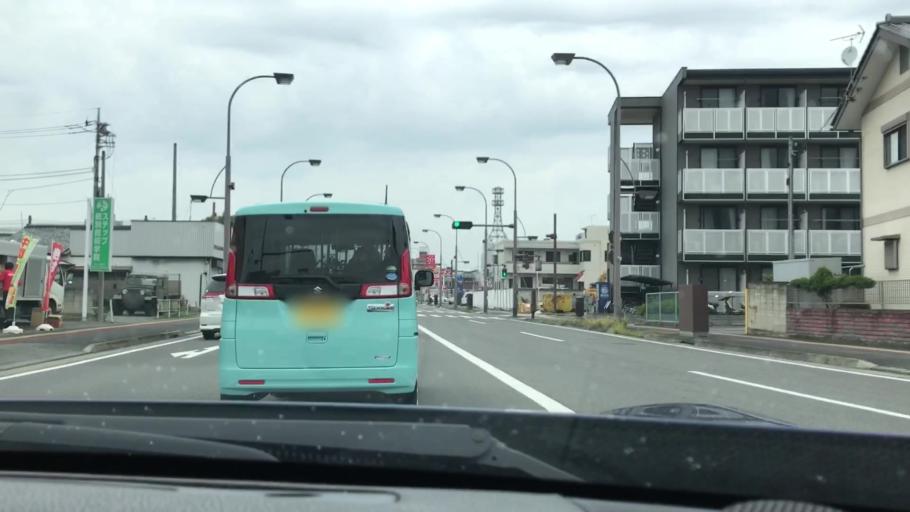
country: JP
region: Gunma
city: Maebashi-shi
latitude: 36.3768
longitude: 139.0701
